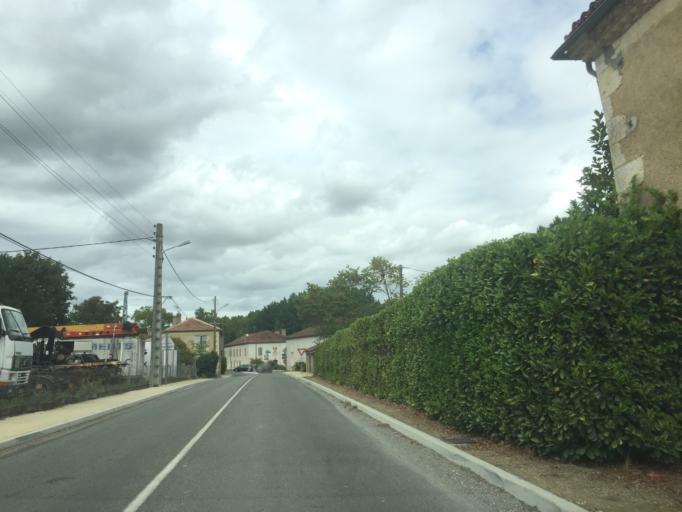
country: FR
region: Midi-Pyrenees
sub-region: Departement du Gers
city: Vic-Fezensac
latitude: 43.7227
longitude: 0.3797
